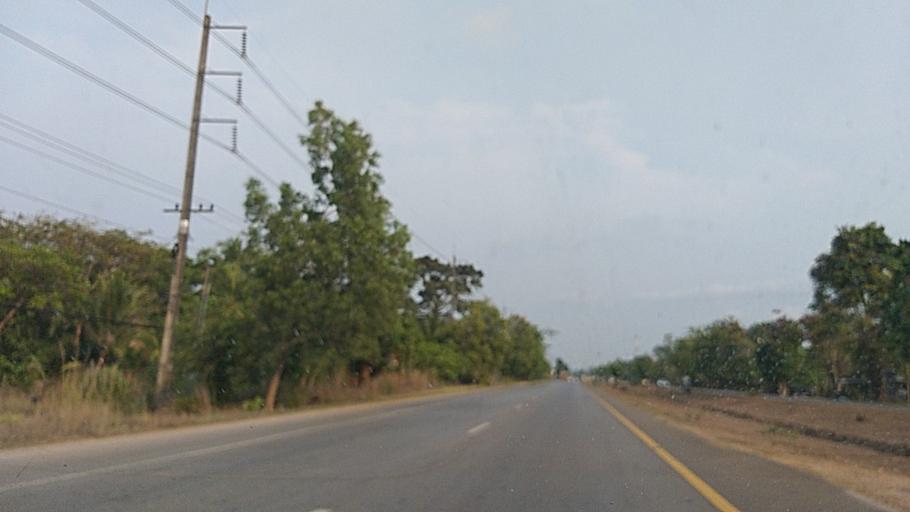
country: TH
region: Trat
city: Khao Saming
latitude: 12.4074
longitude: 102.3372
